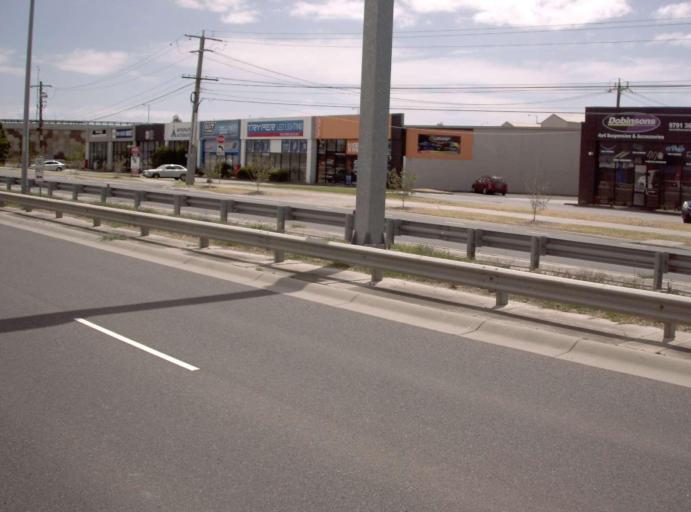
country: AU
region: Victoria
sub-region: Greater Dandenong
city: Dandenong
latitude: -37.9920
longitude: 145.1944
